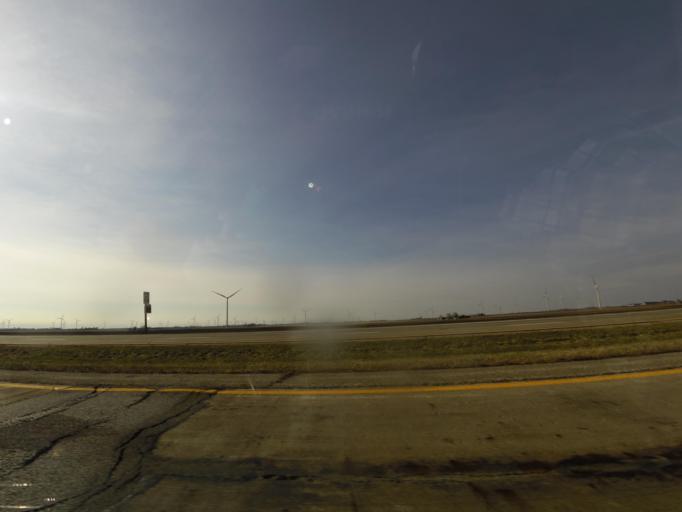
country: US
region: Illinois
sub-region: Macon County
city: Maroa
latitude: 40.0322
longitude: -88.9637
